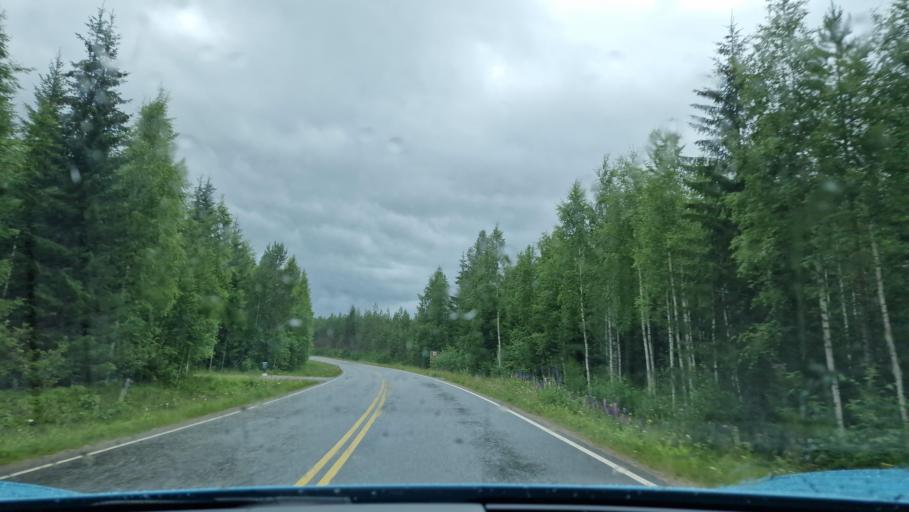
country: FI
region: Southern Ostrobothnia
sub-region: Jaerviseutu
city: Soini
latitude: 62.7839
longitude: 24.3875
